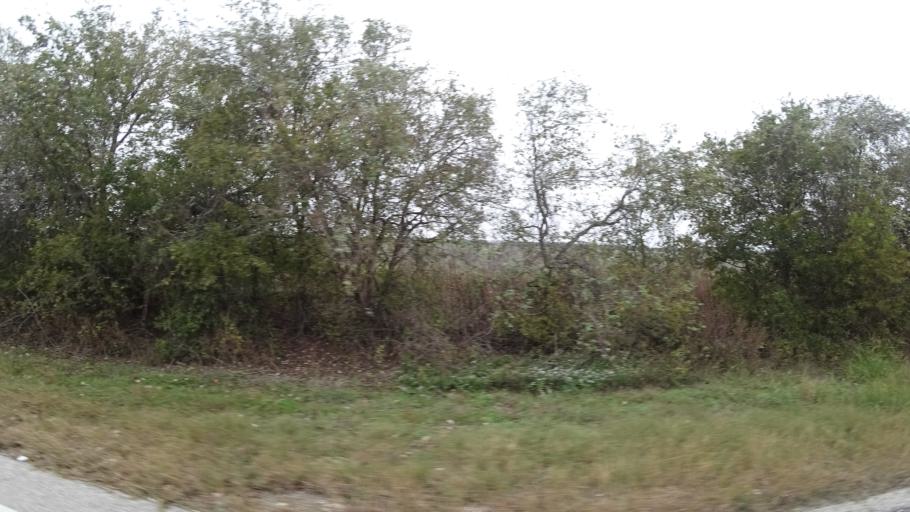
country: US
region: Texas
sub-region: Travis County
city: Pflugerville
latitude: 30.3911
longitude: -97.5975
